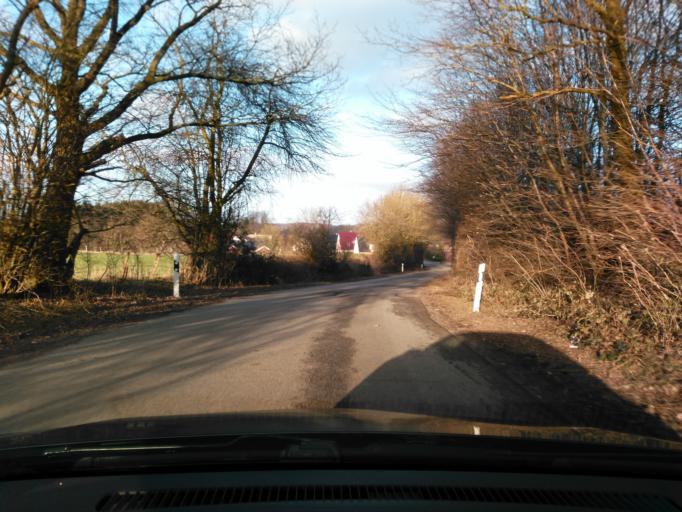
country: DE
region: Schleswig-Holstein
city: Grossbarkau
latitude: 54.2656
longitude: 10.1731
